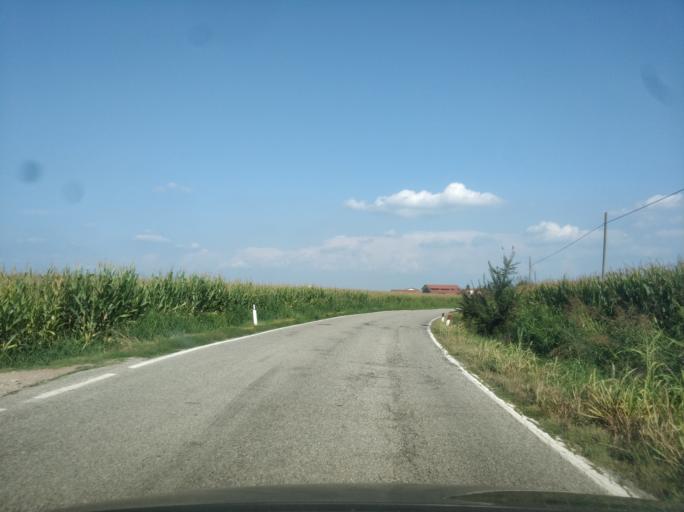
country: IT
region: Piedmont
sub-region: Provincia di Cuneo
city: Centallo
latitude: 44.5336
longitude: 7.6323
